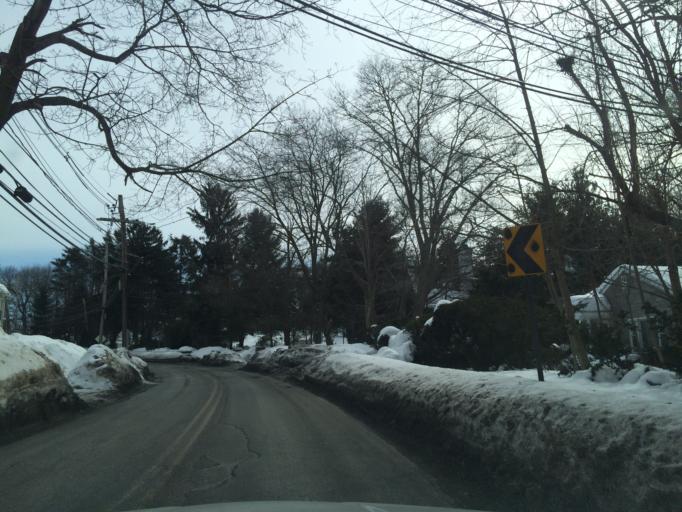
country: US
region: Massachusetts
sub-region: Norfolk County
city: Needham
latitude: 42.3098
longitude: -71.2236
